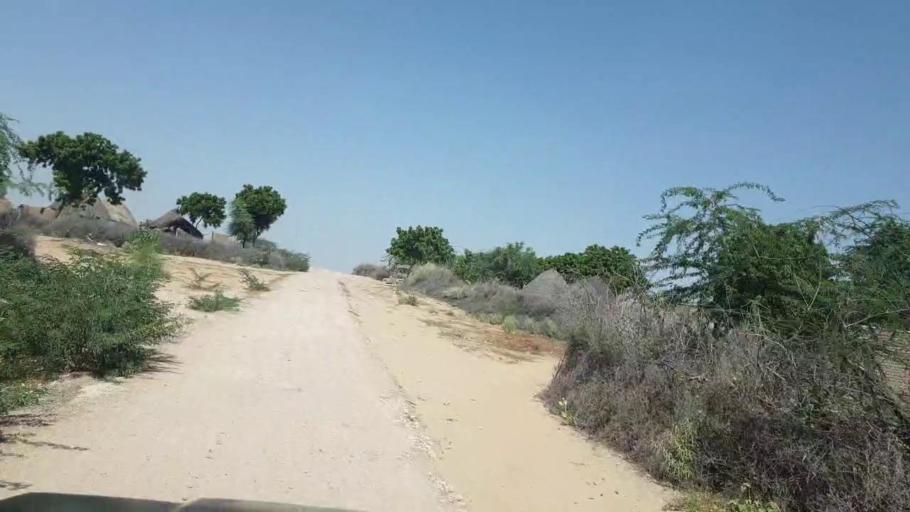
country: PK
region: Sindh
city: Chor
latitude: 25.3769
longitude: 70.3150
